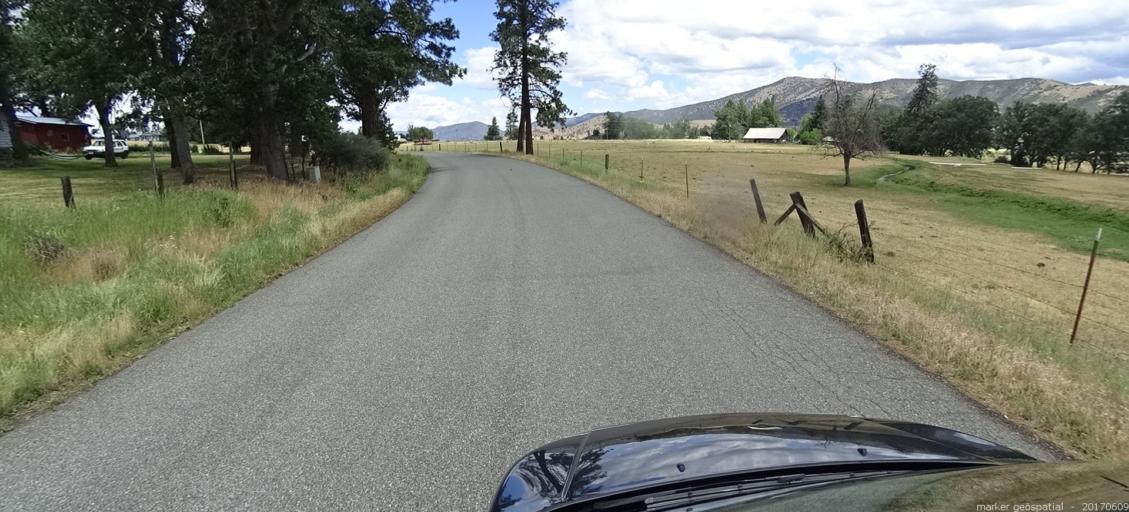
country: US
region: California
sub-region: Siskiyou County
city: Yreka
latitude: 41.4113
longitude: -122.8636
